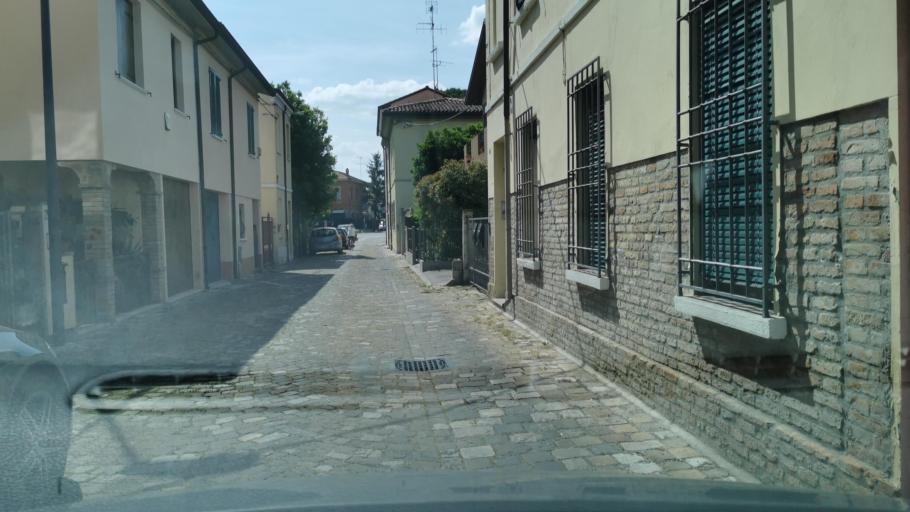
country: IT
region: Emilia-Romagna
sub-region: Provincia di Ravenna
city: Ravenna
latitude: 44.4096
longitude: 12.1991
